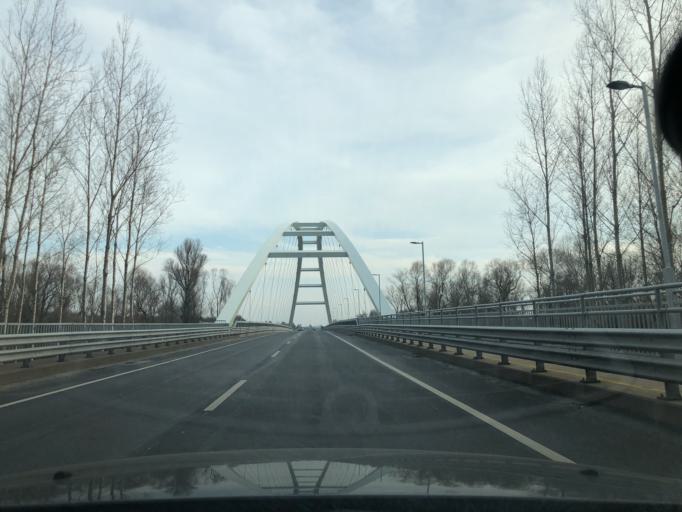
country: HU
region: Gyor-Moson-Sopron
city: Gyor
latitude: 47.7282
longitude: 17.7003
